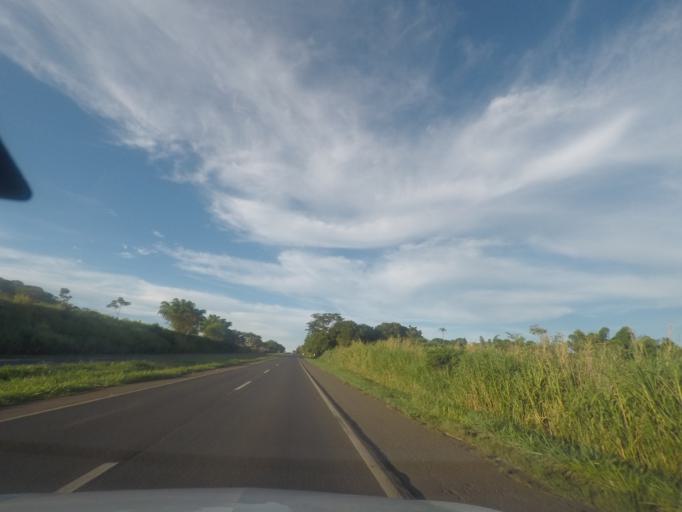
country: BR
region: Goias
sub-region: Goiatuba
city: Goiatuba
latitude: -18.1226
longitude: -49.2821
